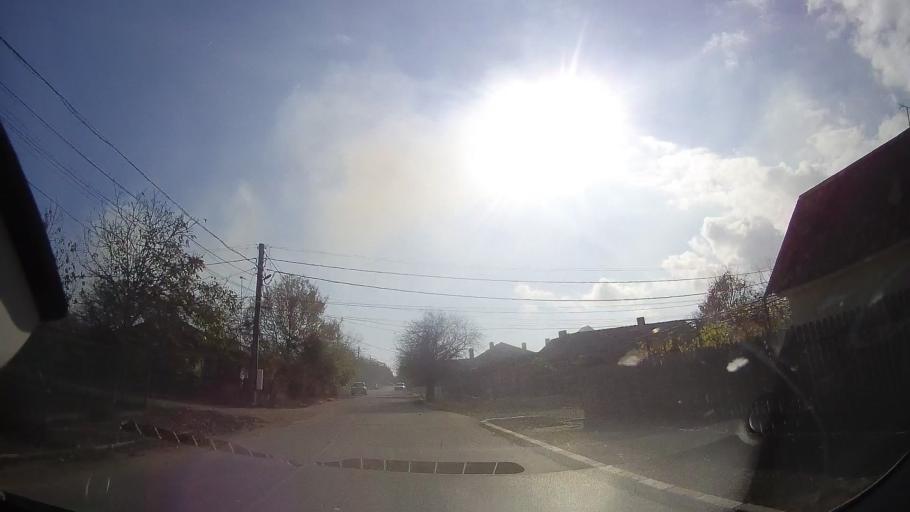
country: RO
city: Eforie Sud
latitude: 44.0115
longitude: 28.6442
